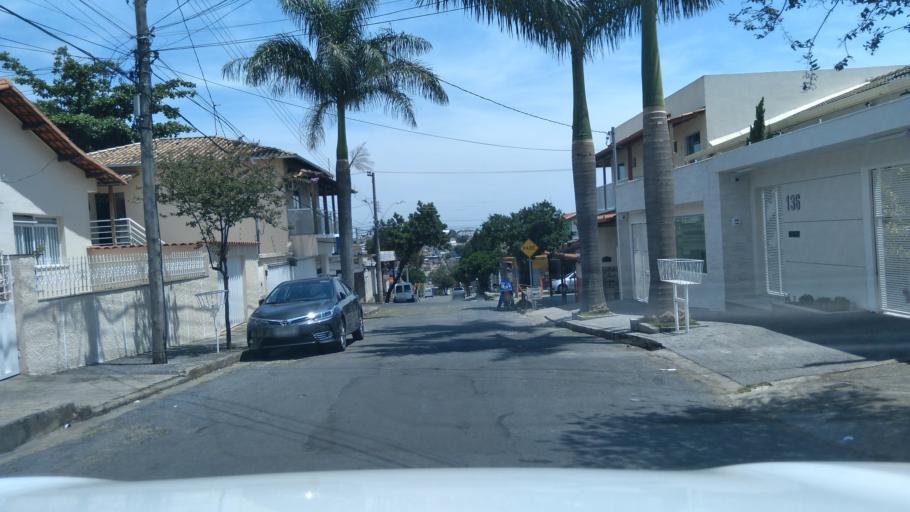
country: BR
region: Minas Gerais
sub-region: Contagem
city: Contagem
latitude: -19.9022
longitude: -44.0145
